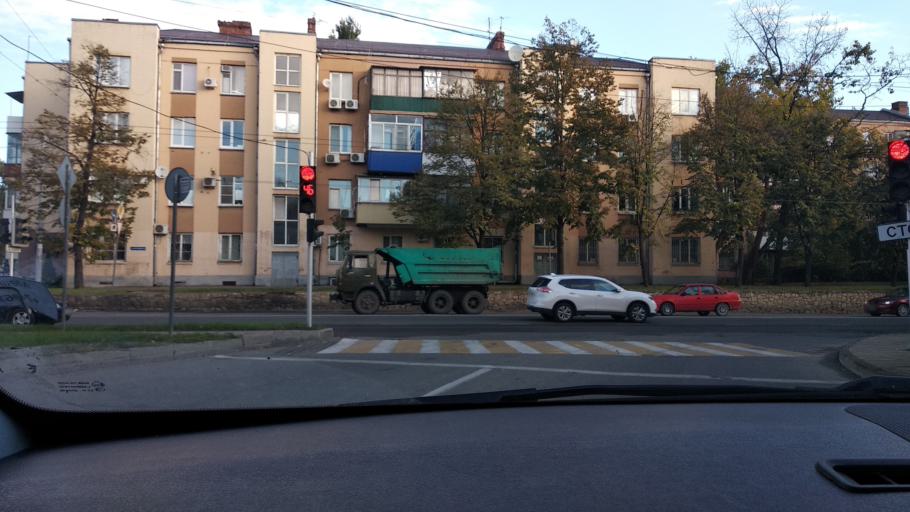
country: RU
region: Krasnodarskiy
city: Krasnodar
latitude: 45.0135
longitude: 38.9739
